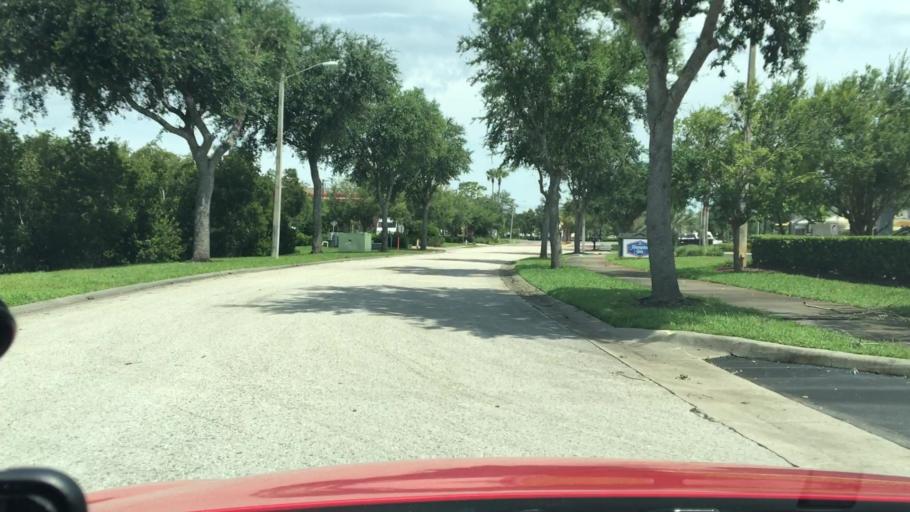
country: US
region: Florida
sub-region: Volusia County
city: Ormond Beach
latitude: 29.2544
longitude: -81.1180
